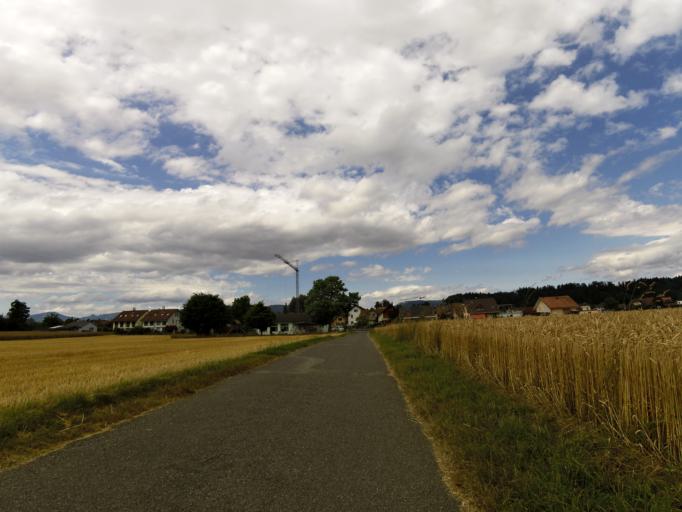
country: CH
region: Bern
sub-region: Oberaargau
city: Aarwangen
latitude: 47.2333
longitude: 7.7834
